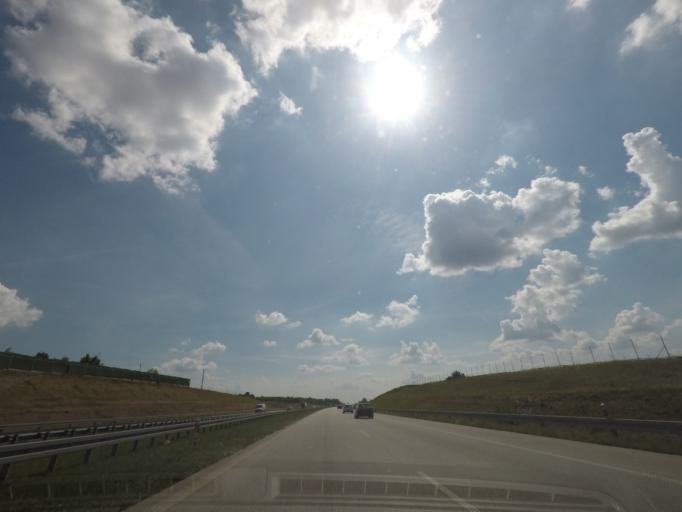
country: PL
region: Lodz Voivodeship
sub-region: Powiat zgierski
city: Strykow
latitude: 51.8211
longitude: 19.6466
